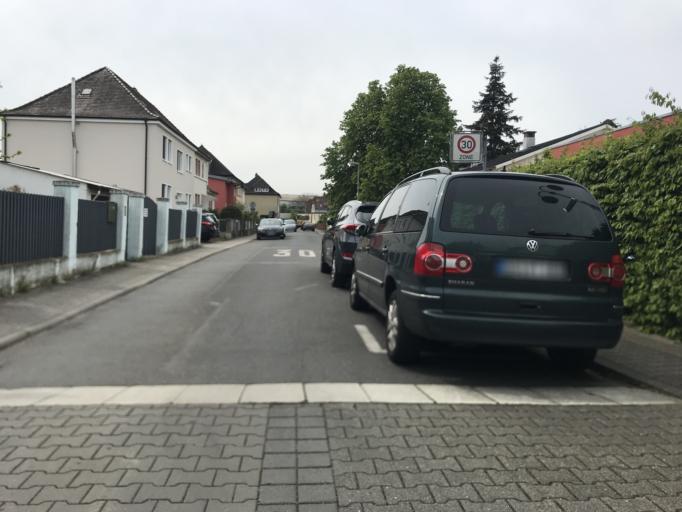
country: DE
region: Hesse
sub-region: Regierungsbezirk Darmstadt
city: Hochheim am Main
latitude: 49.9968
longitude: 8.3300
